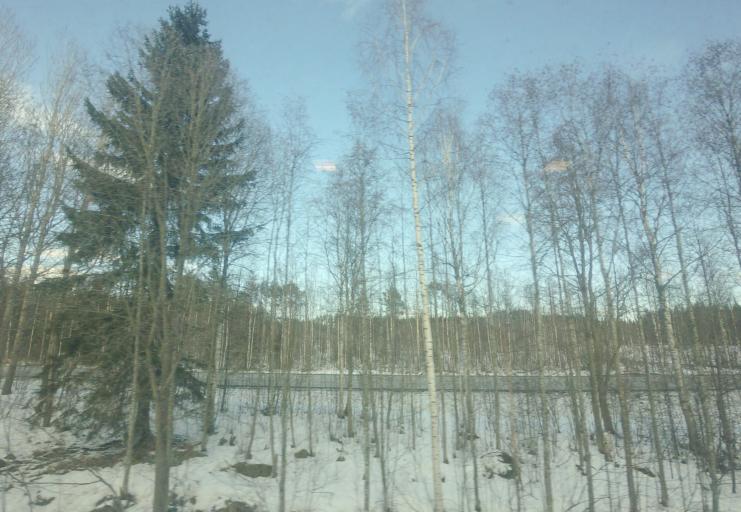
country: FI
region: Southern Savonia
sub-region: Savonlinna
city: Punkaharju
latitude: 61.7837
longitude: 29.3474
